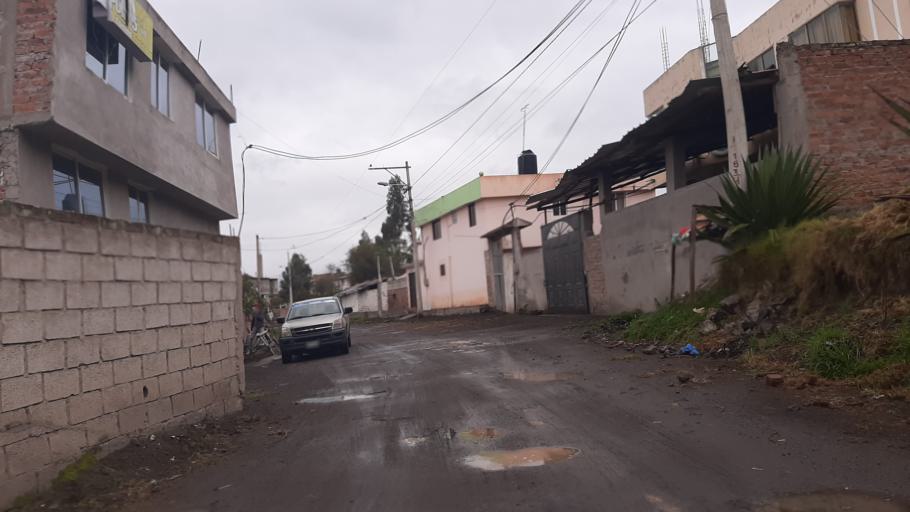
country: EC
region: Chimborazo
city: Riobamba
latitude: -1.6497
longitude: -78.6365
